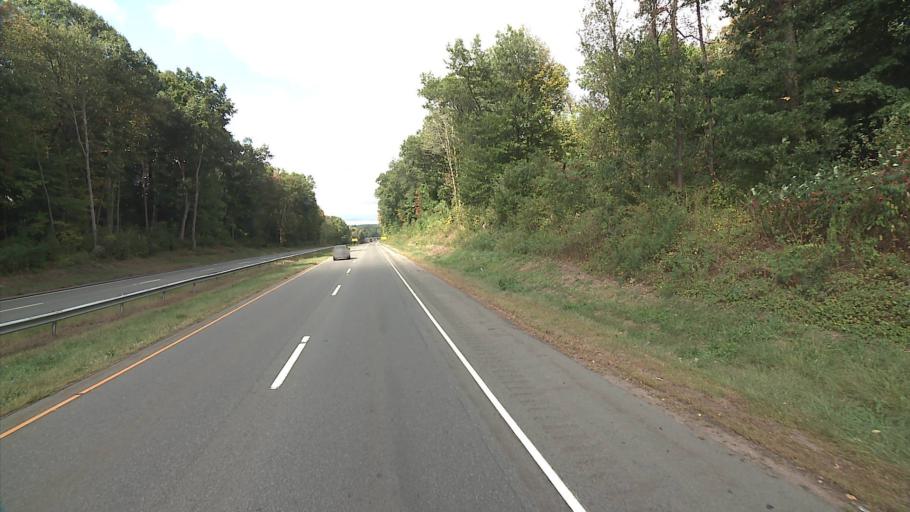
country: US
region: Connecticut
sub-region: New Haven County
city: Meriden
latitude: 41.5521
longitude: -72.7741
